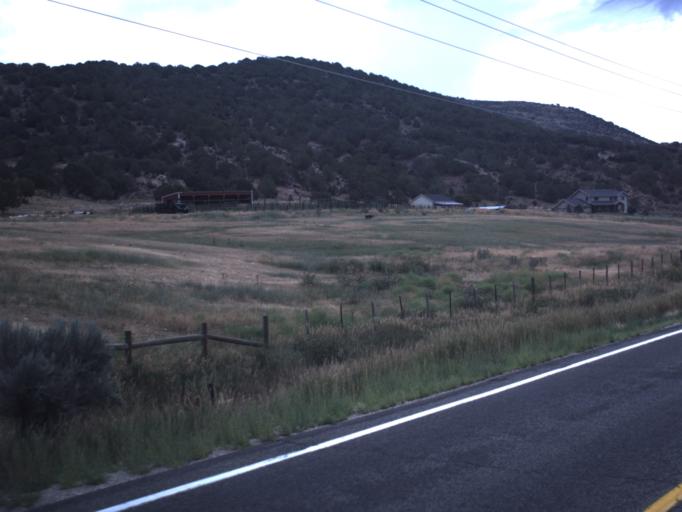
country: US
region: Utah
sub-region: Summit County
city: Oakley
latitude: 40.7467
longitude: -111.3616
